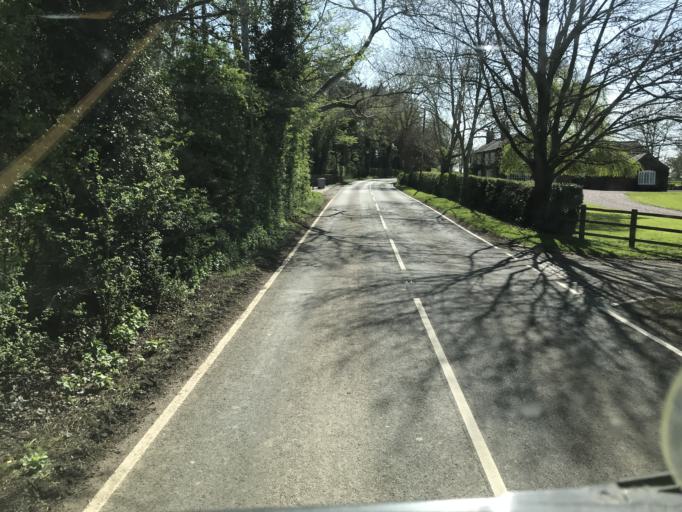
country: GB
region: England
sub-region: Cheshire East
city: Nantwich
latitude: 53.0957
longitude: -2.5135
